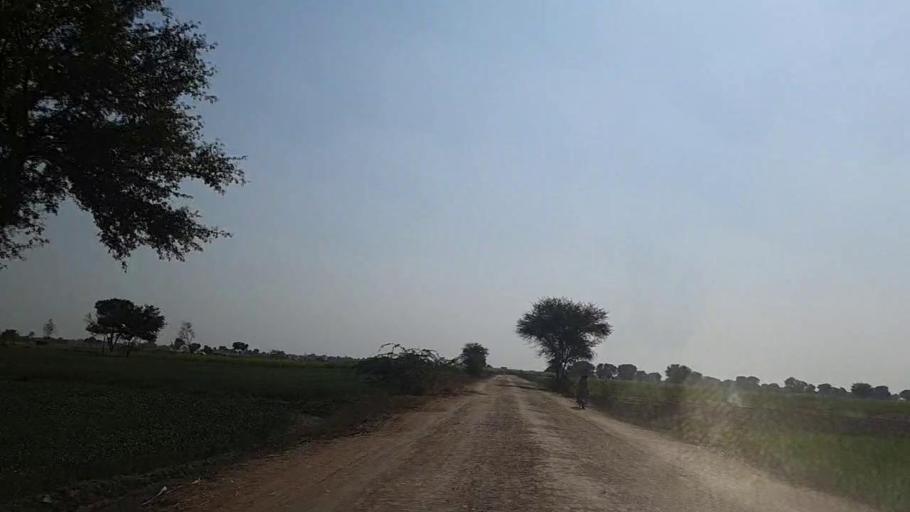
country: PK
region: Sindh
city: Daur
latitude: 26.4723
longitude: 68.2509
